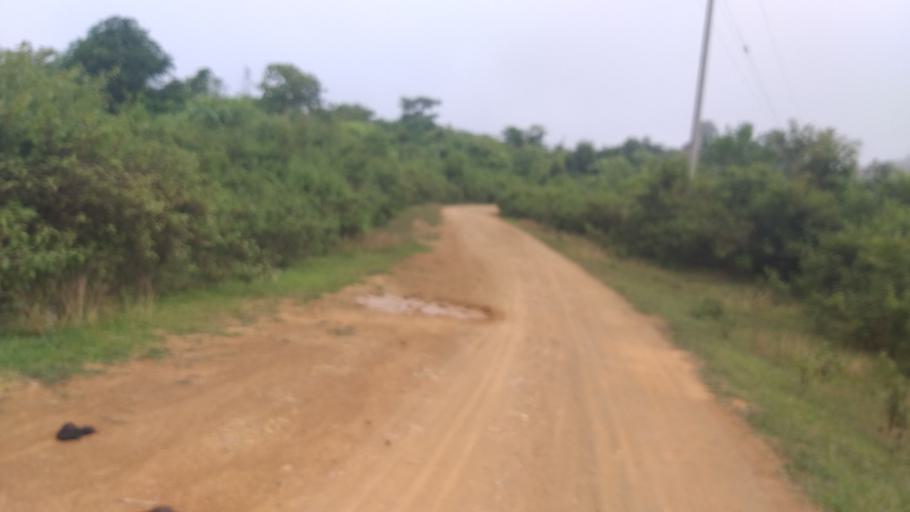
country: LA
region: Phongsali
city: Khoa
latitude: 21.2834
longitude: 102.6416
